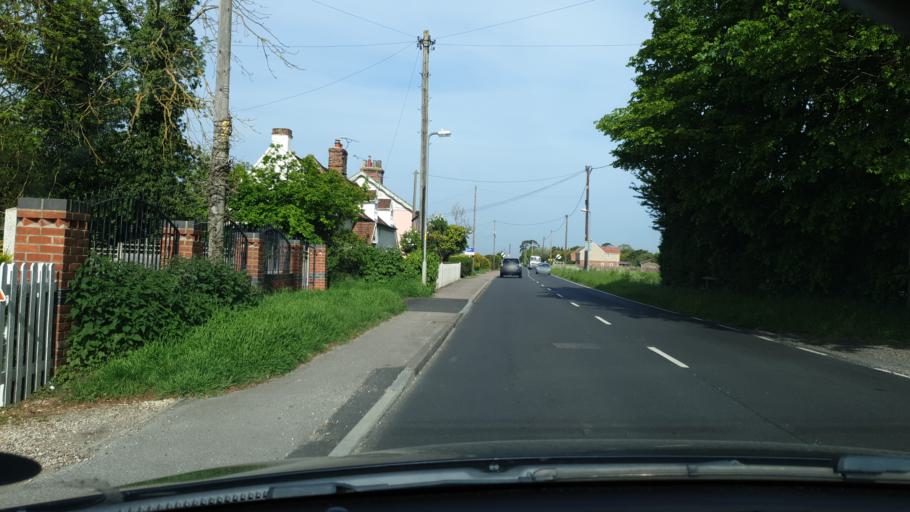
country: GB
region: England
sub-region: Essex
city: Frinton-on-Sea
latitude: 51.8455
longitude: 1.2008
